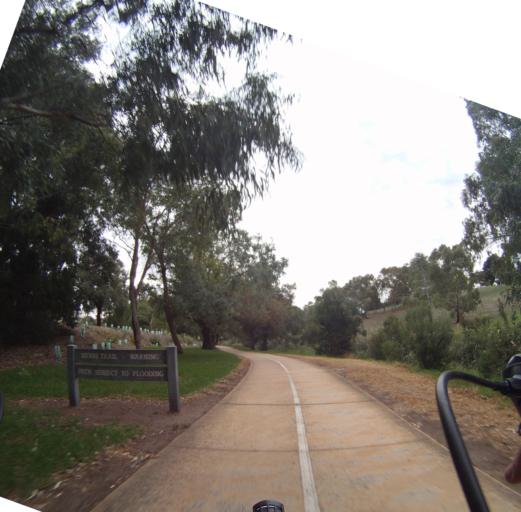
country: AU
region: Victoria
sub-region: Moreland
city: Coburg North
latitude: -37.7304
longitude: 144.9678
